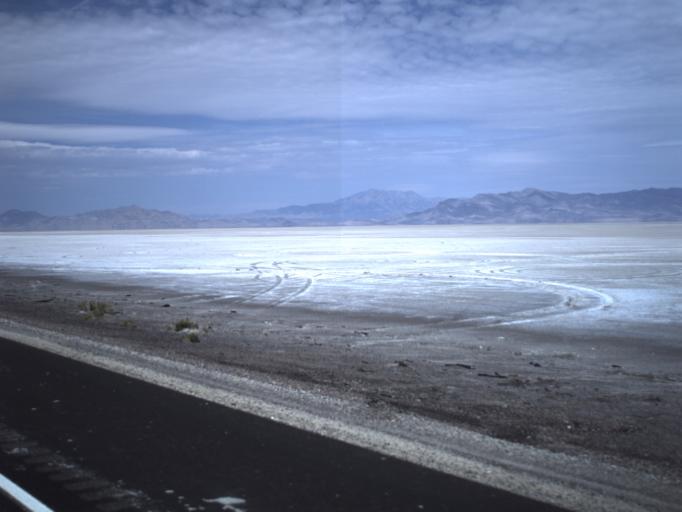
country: US
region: Utah
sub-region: Tooele County
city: Wendover
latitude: 40.7350
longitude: -113.6424
